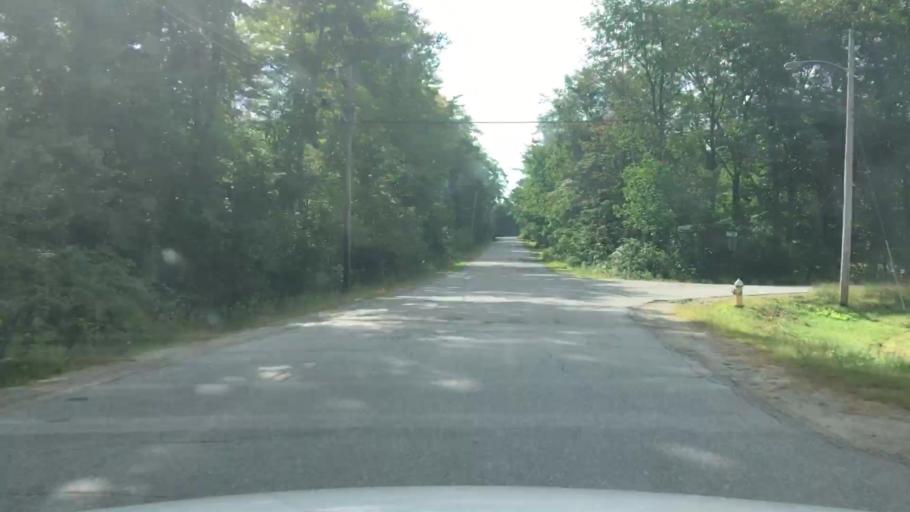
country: US
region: Maine
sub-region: Kennebec County
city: Gardiner
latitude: 44.1734
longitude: -69.8193
